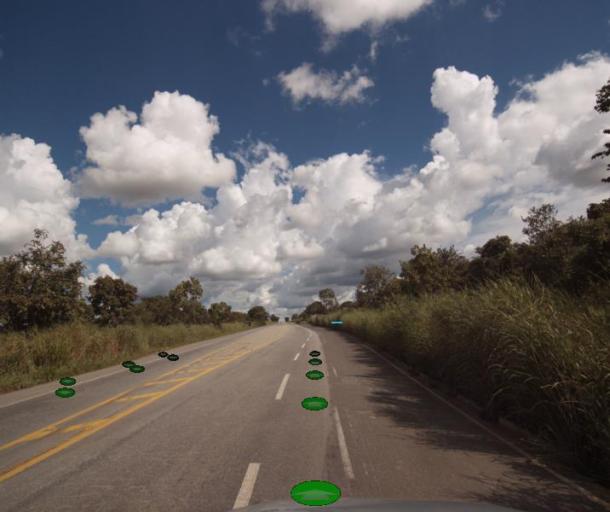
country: BR
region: Goias
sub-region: Porangatu
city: Porangatu
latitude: -13.4146
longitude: -49.1315
